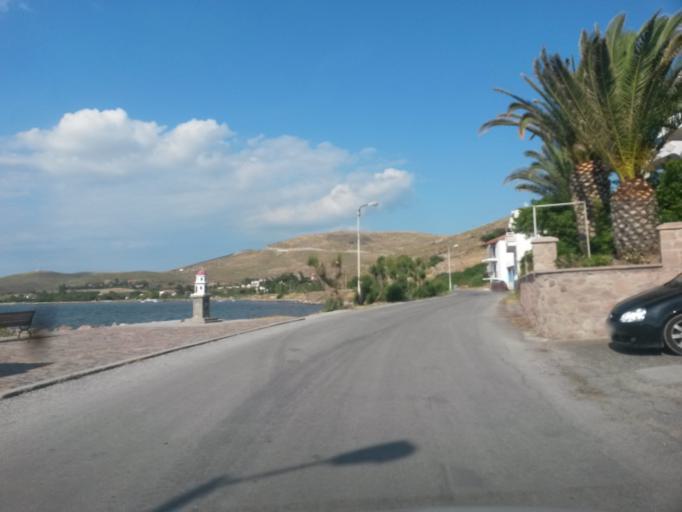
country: GR
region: North Aegean
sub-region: Nomos Lesvou
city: Eresos
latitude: 39.2126
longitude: 25.8523
